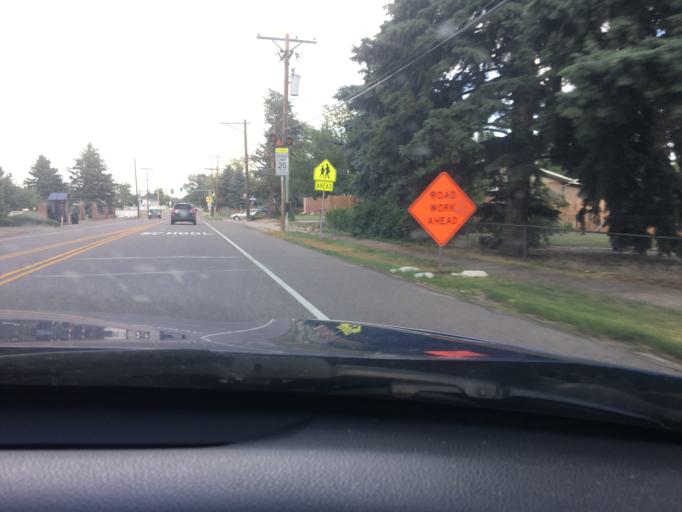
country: US
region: Colorado
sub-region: Jefferson County
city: Applewood
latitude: 39.7675
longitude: -105.1388
